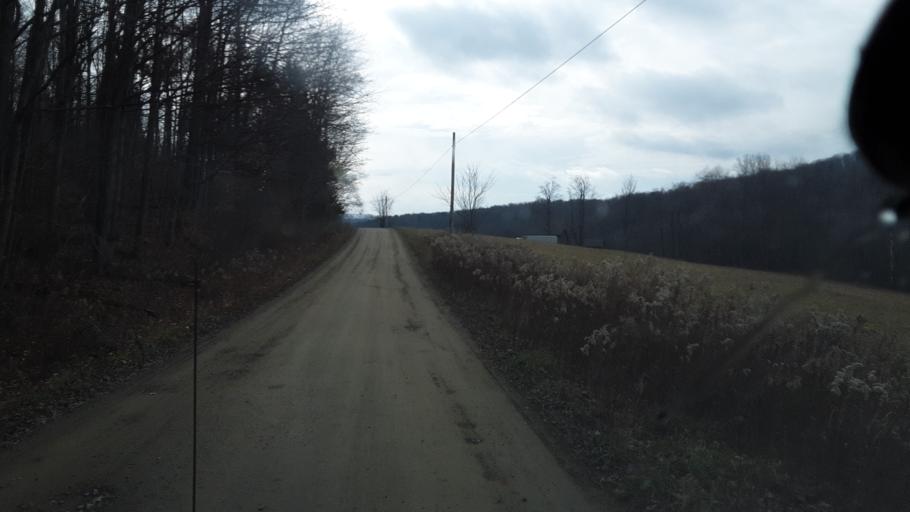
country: US
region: Pennsylvania
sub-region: Tioga County
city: Westfield
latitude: 41.9161
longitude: -77.7185
